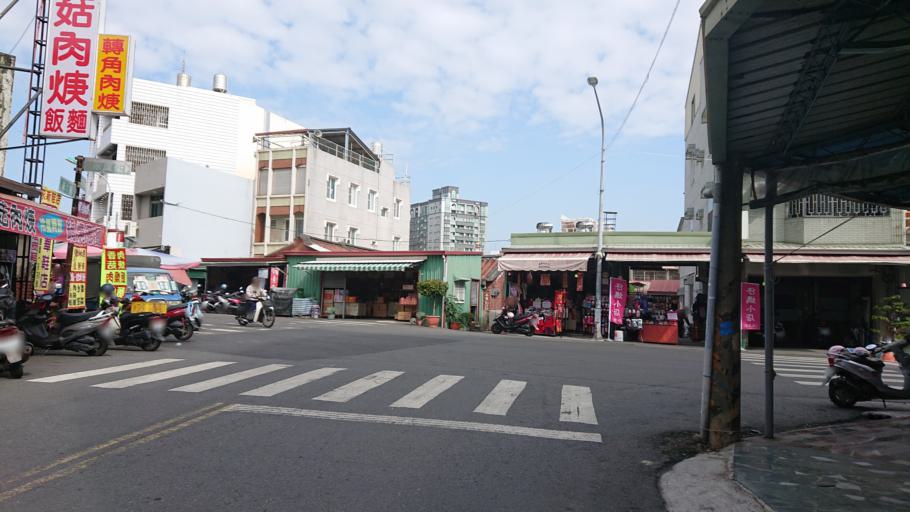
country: TW
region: Taiwan
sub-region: Tainan
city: Tainan
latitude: 23.0241
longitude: 120.2566
